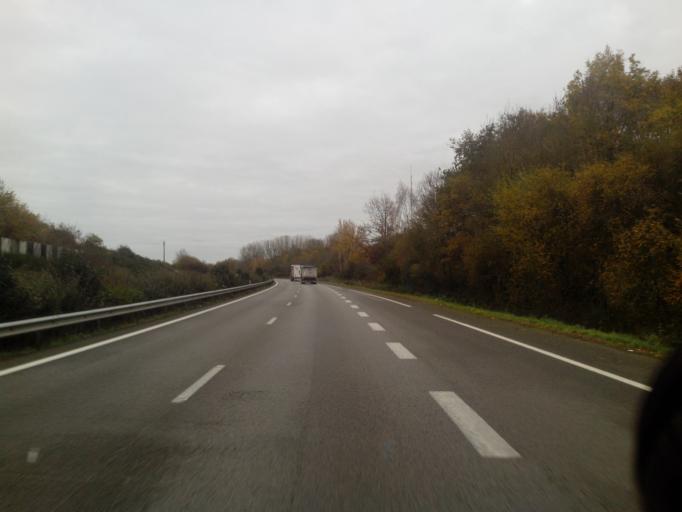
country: FR
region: Pays de la Loire
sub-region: Departement de la Loire-Atlantique
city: Haute-Goulaine
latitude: 47.1975
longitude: -1.4461
